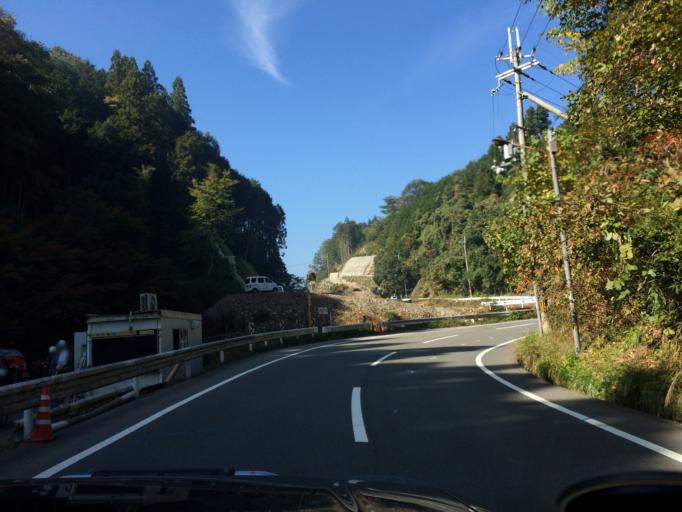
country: JP
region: Kyoto
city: Kameoka
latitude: 35.0526
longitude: 135.5264
